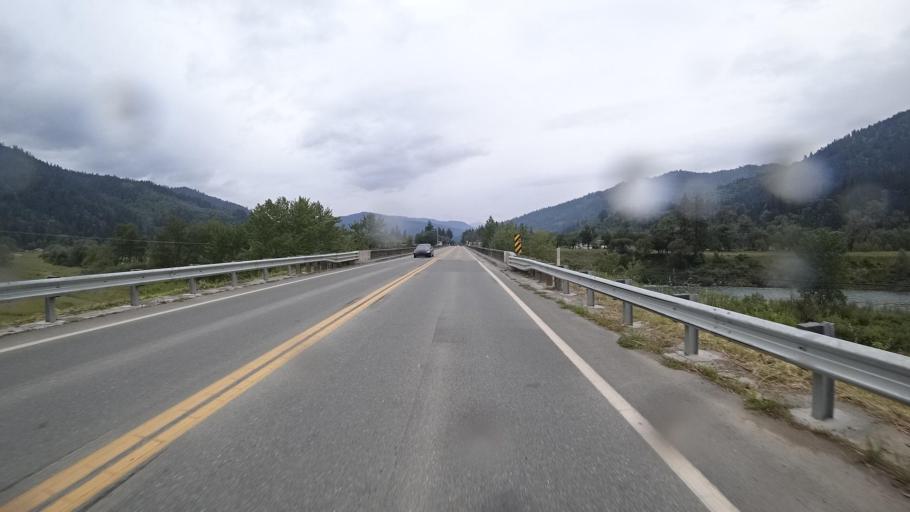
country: US
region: California
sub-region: Humboldt County
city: Willow Creek
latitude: 41.0598
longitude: -123.6848
